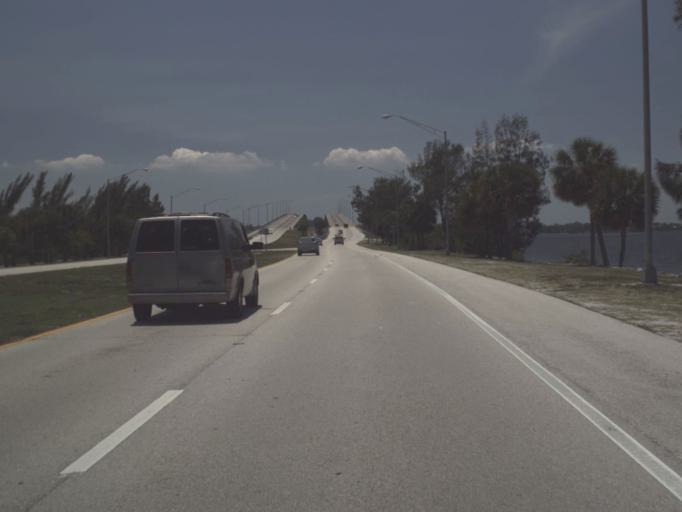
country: US
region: Florida
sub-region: Brevard County
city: Indialantic
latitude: 28.0871
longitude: -80.5833
